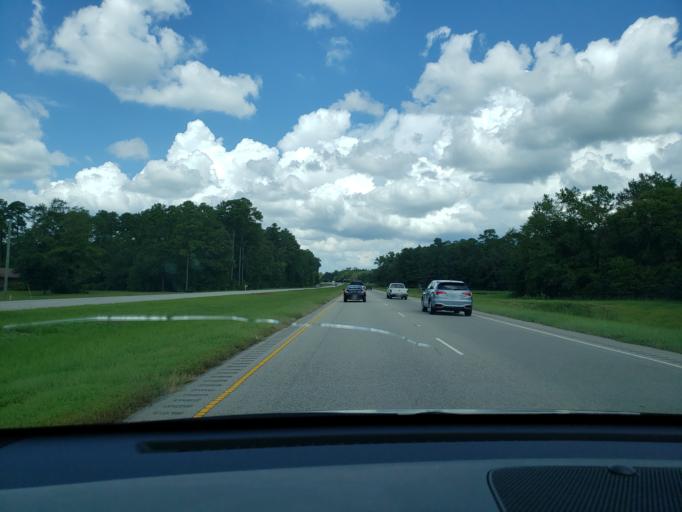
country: US
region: North Carolina
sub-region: Bladen County
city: Elizabethtown
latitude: 34.6960
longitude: -78.7400
